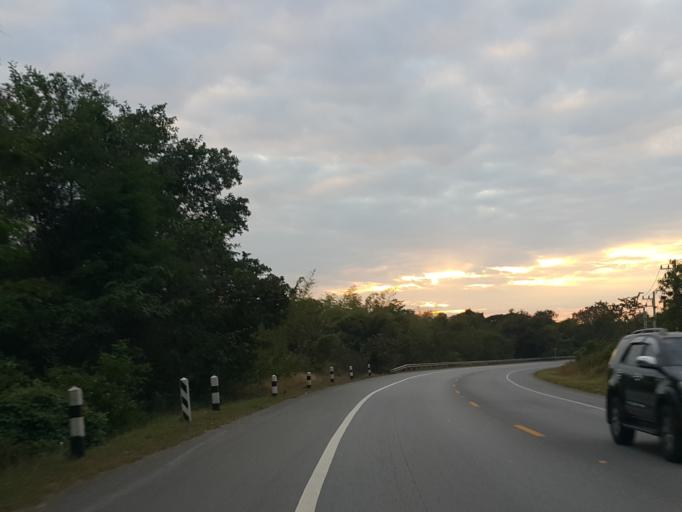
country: TH
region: Lampang
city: Lampang
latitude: 18.2517
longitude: 99.5374
